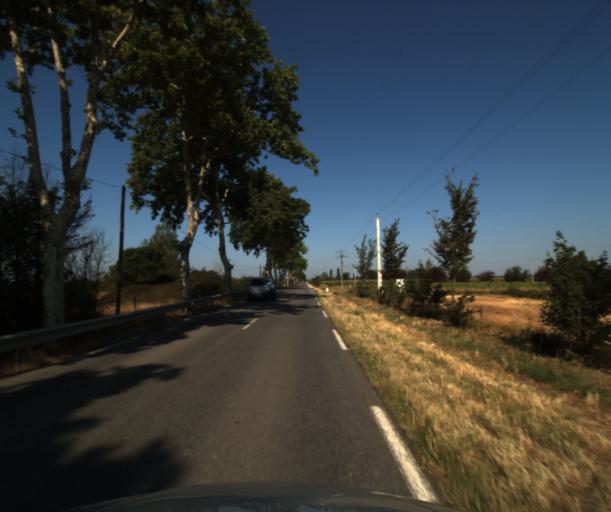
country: FR
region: Midi-Pyrenees
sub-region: Departement de la Haute-Garonne
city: Labastidette
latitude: 43.4663
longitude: 1.2637
